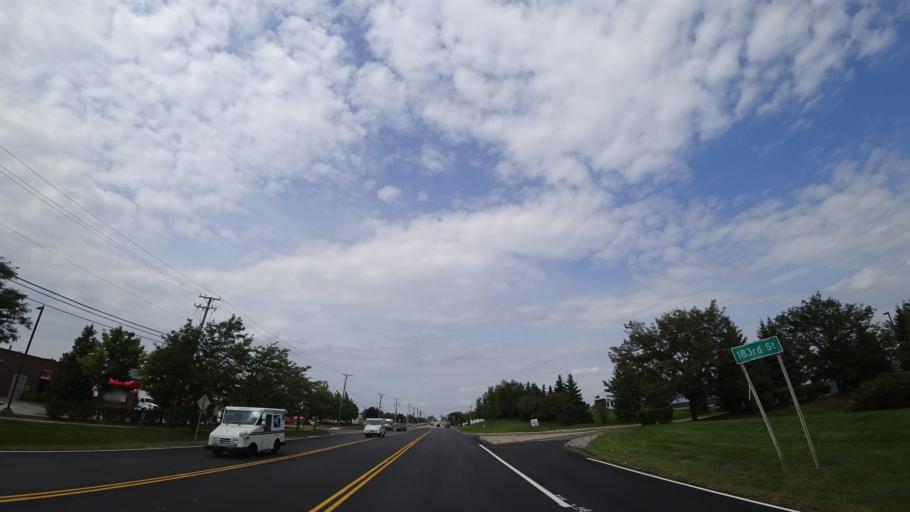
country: US
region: Illinois
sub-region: Cook County
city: Tinley Park
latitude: 41.5562
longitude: -87.8121
